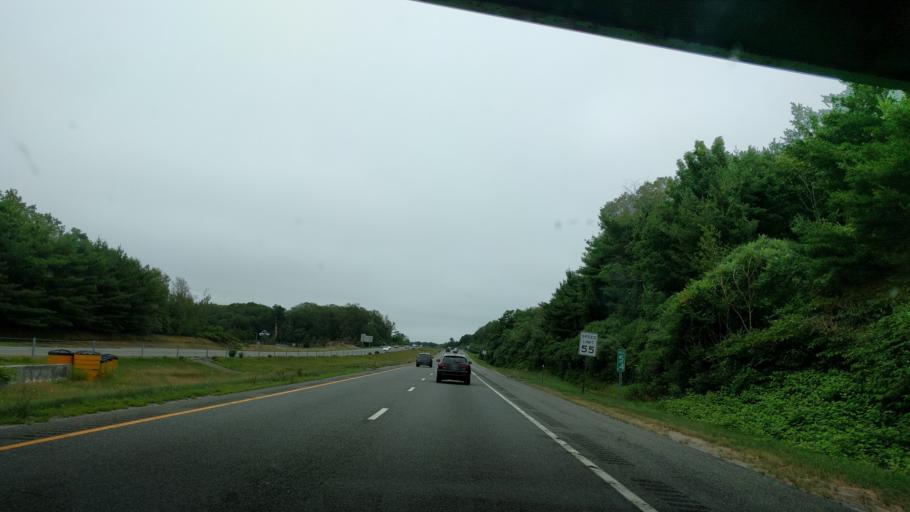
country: US
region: Rhode Island
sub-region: Washington County
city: Exeter
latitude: 41.6082
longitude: -71.4964
